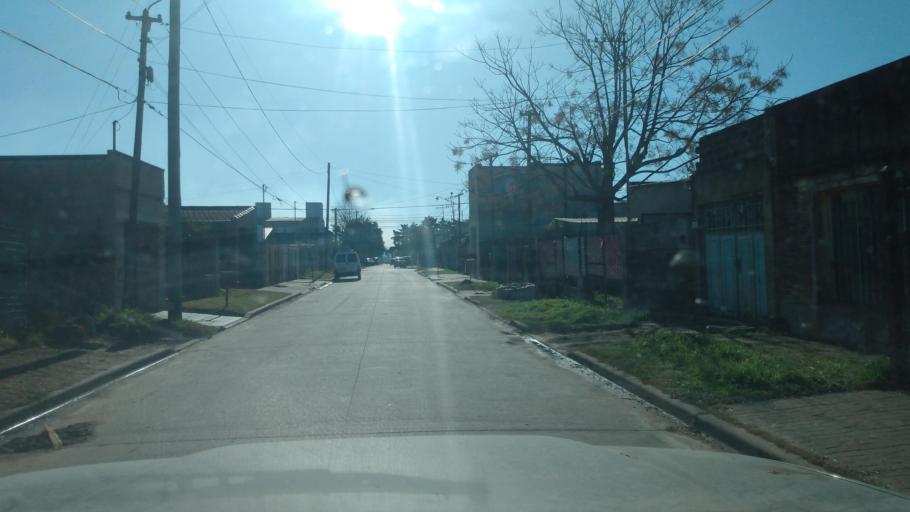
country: AR
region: Buenos Aires
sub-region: Partido de Lujan
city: Lujan
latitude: -34.5643
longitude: -59.0921
